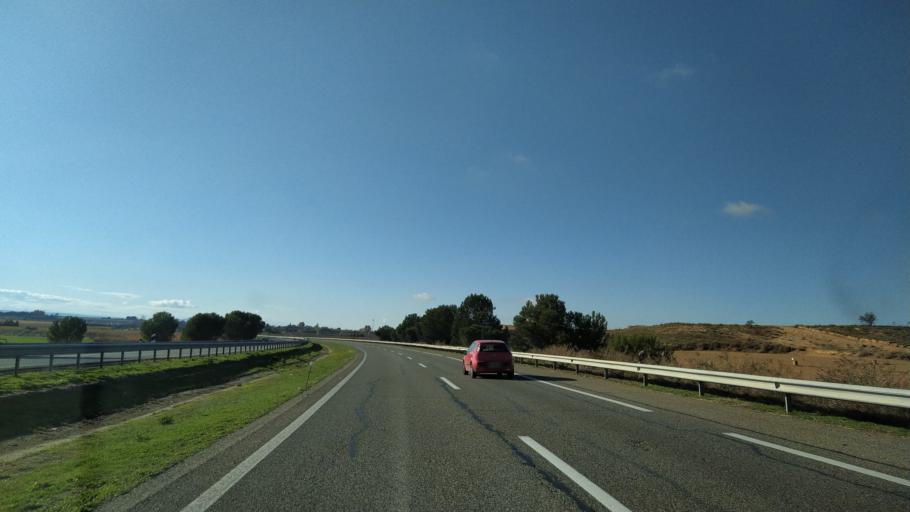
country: ES
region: Catalonia
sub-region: Provincia de Lleida
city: Alcarras
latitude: 41.6016
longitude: 0.5276
